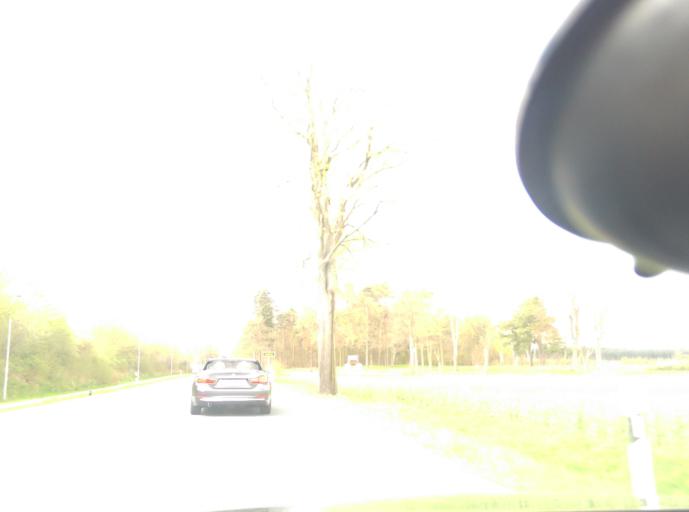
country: DE
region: Lower Saxony
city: Hambuhren
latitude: 52.6348
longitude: 9.9717
